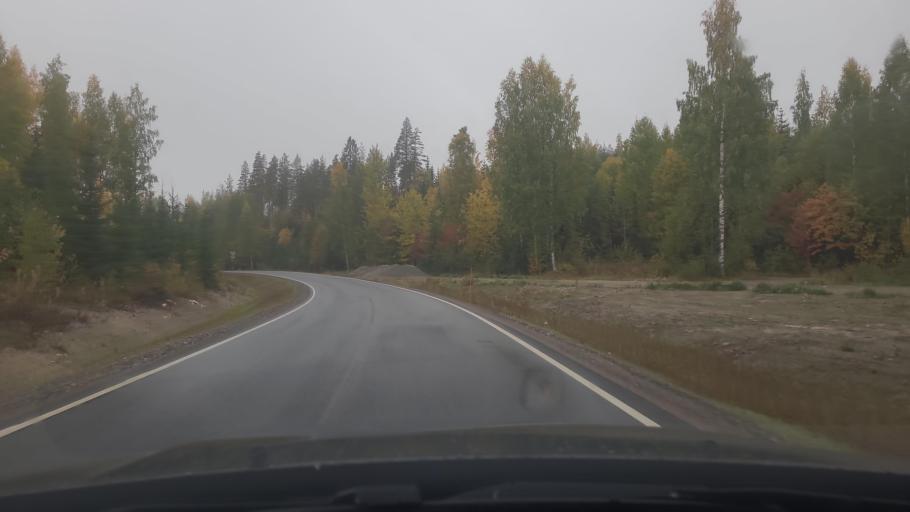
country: FI
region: Northern Savo
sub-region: Varkaus
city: Kangaslampi
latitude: 62.4536
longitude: 28.2815
